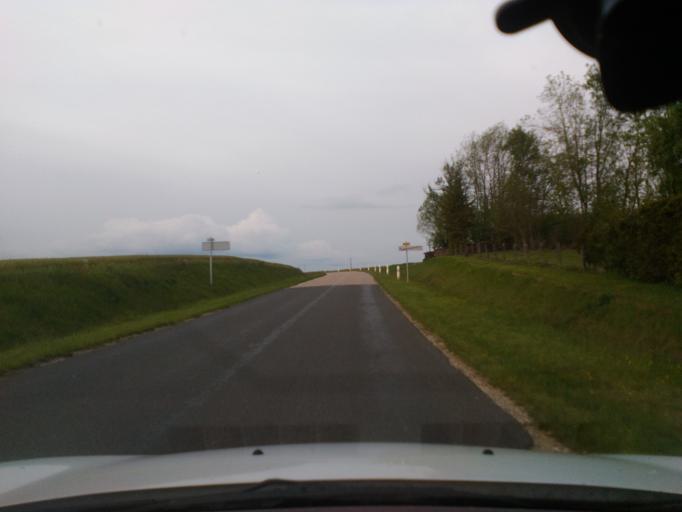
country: FR
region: Champagne-Ardenne
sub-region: Departement de la Haute-Marne
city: Doulaincourt-Saucourt
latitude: 48.2249
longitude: 5.2616
